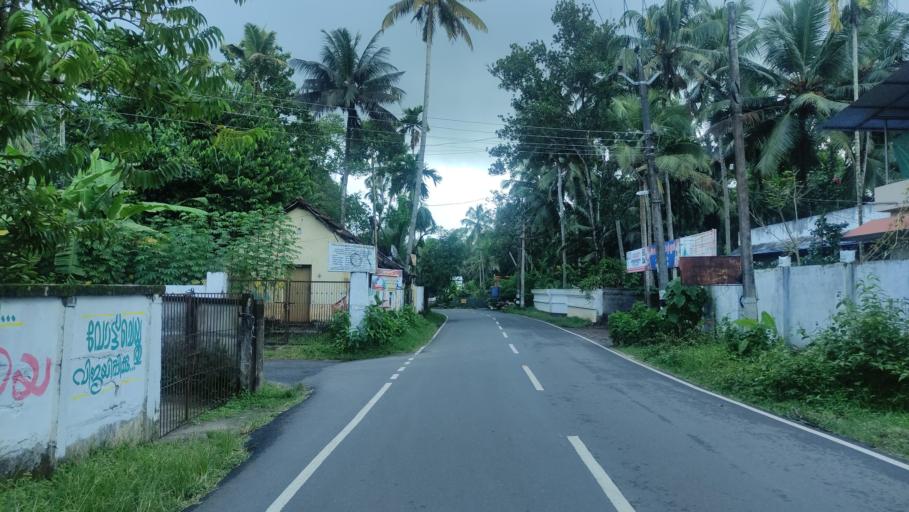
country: IN
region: Kerala
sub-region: Alappuzha
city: Kayankulam
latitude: 9.1944
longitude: 76.5023
